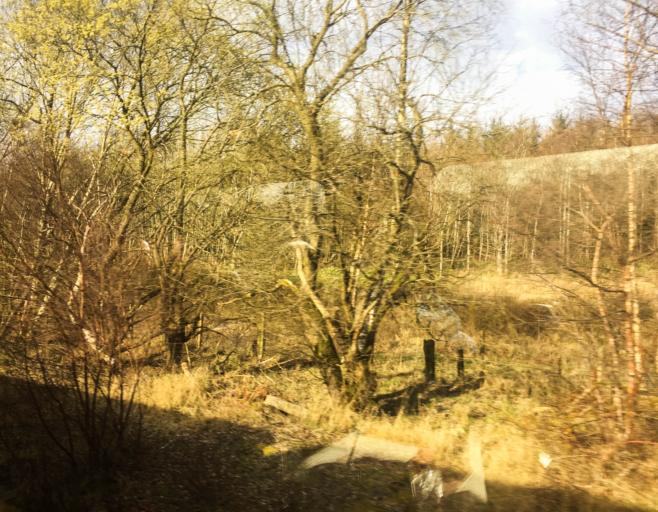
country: GB
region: Scotland
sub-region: North Lanarkshire
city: Glenboig
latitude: 55.8793
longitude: -4.0495
